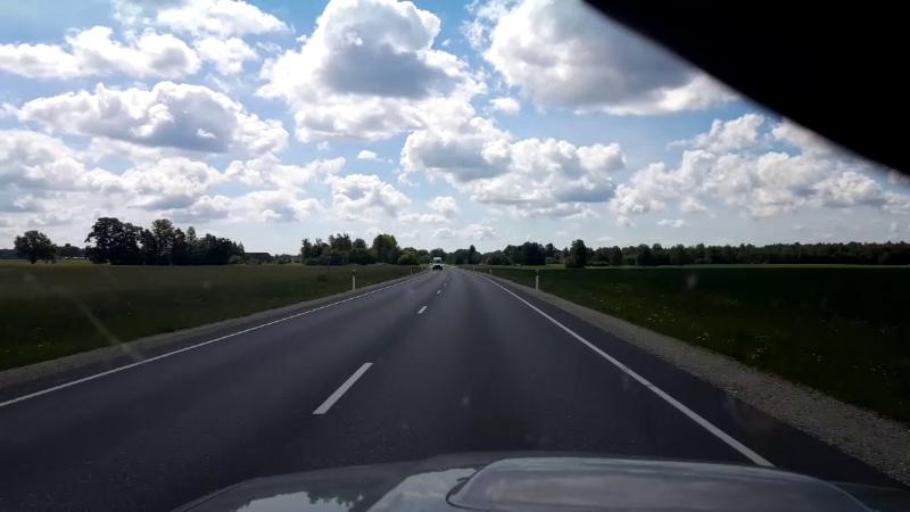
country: EE
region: Jaervamaa
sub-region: Jaerva-Jaani vald
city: Jarva-Jaani
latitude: 59.0792
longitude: 25.6836
